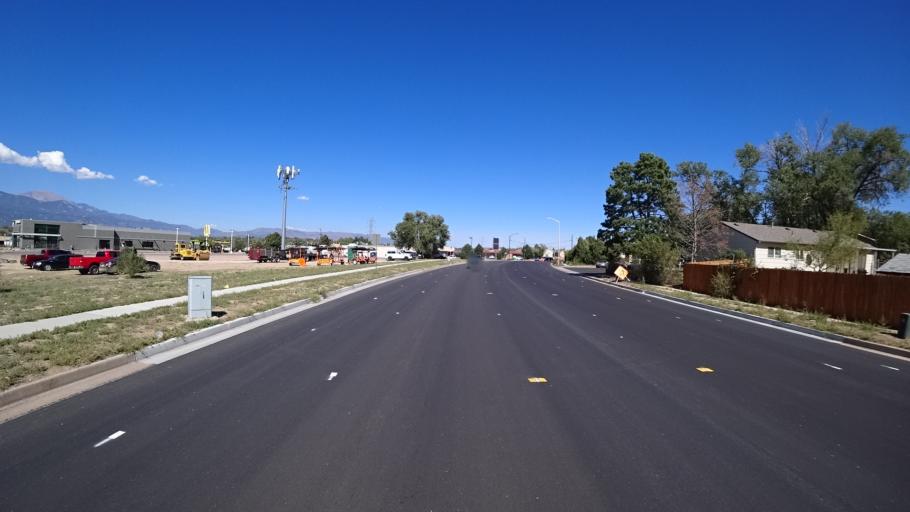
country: US
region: Colorado
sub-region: El Paso County
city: Stratmoor
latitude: 38.7951
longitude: -104.7557
